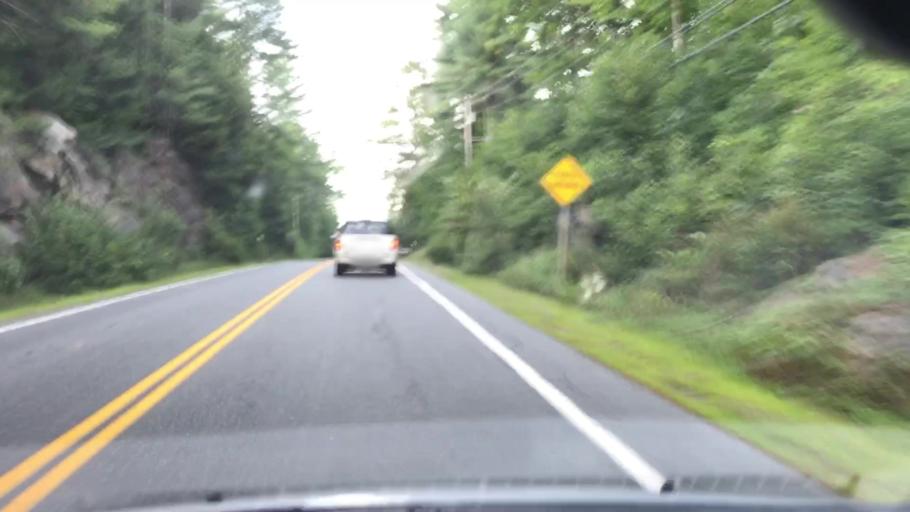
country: US
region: New Hampshire
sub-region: Grafton County
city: Rumney
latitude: 43.8820
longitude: -71.9089
